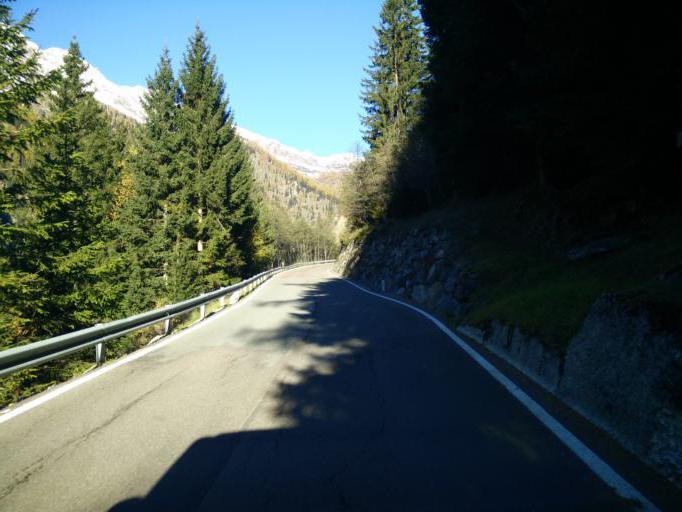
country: IT
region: Trentino-Alto Adige
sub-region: Bolzano
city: Moso in Passiria
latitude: 46.8495
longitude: 11.1648
